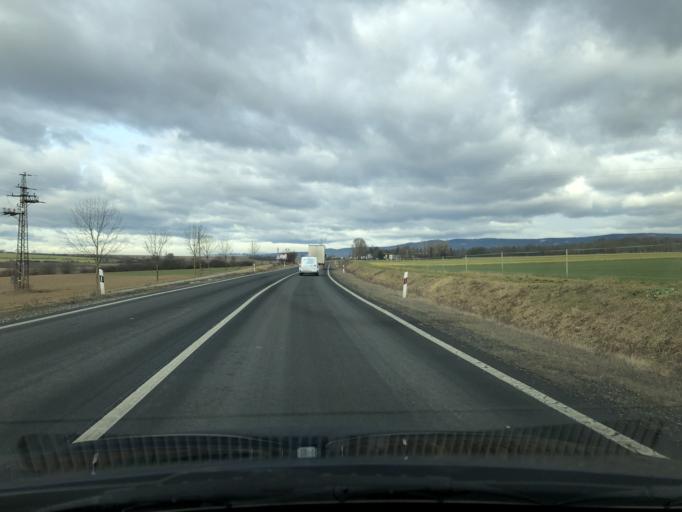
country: AT
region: Burgenland
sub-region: Politischer Bezirk Oberwart
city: Schachendorf
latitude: 47.2497
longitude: 16.4768
